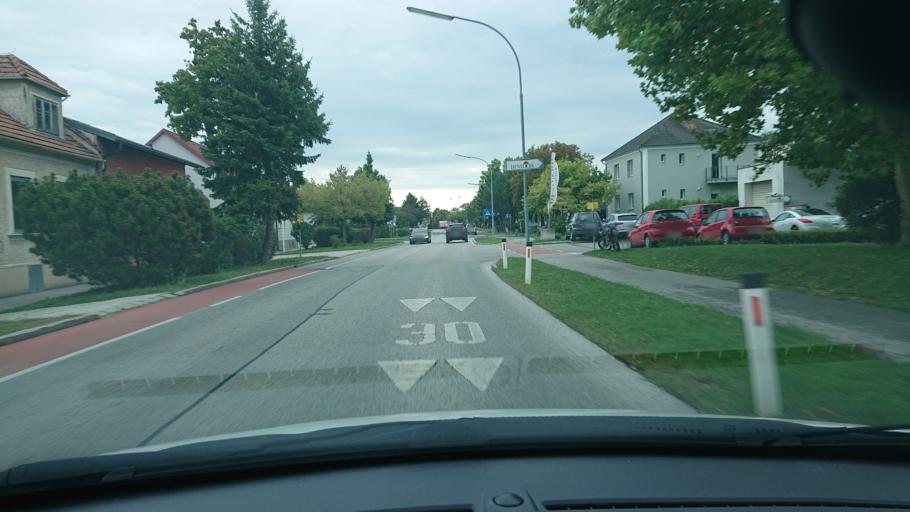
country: AT
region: Lower Austria
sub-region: Wiener Neustadt Stadt
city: Wiener Neustadt
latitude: 47.8087
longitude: 16.2210
